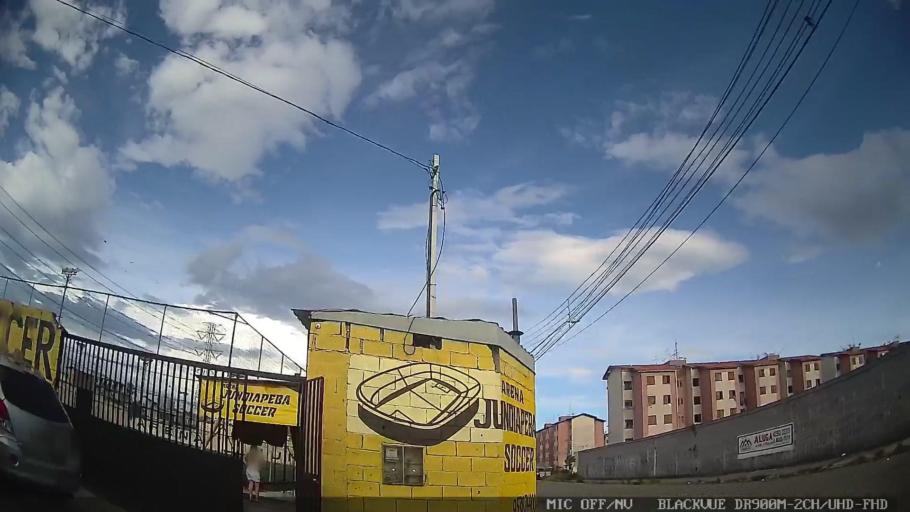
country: BR
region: Sao Paulo
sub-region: Suzano
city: Suzano
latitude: -23.5493
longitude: -46.2478
